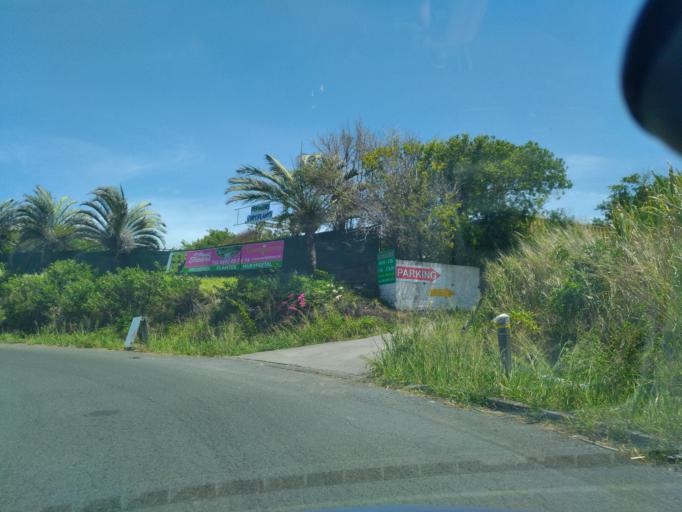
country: RE
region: Reunion
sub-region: Reunion
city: Saint-Pierre
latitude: -21.3265
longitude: 55.4505
